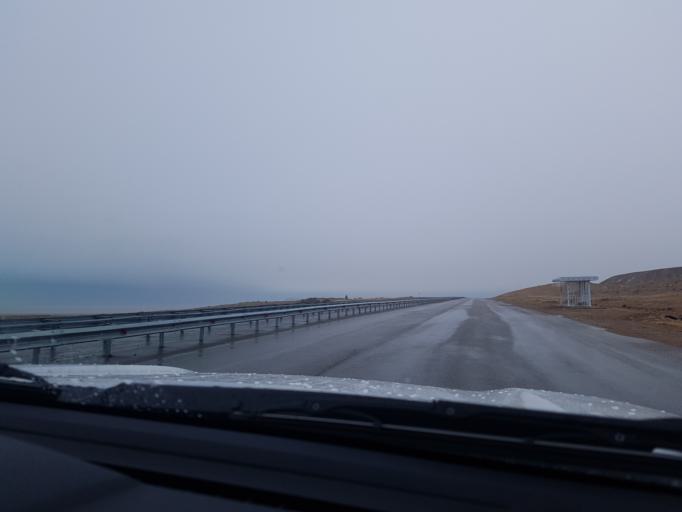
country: TM
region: Balkan
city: Turkmenbasy
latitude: 40.0284
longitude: 53.5090
